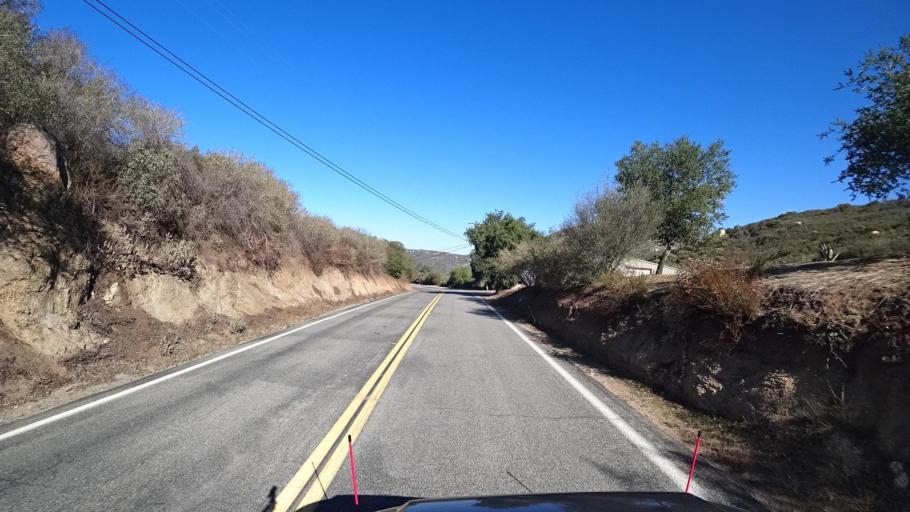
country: US
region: California
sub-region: San Diego County
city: Jamul
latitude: 32.7027
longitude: -116.7455
